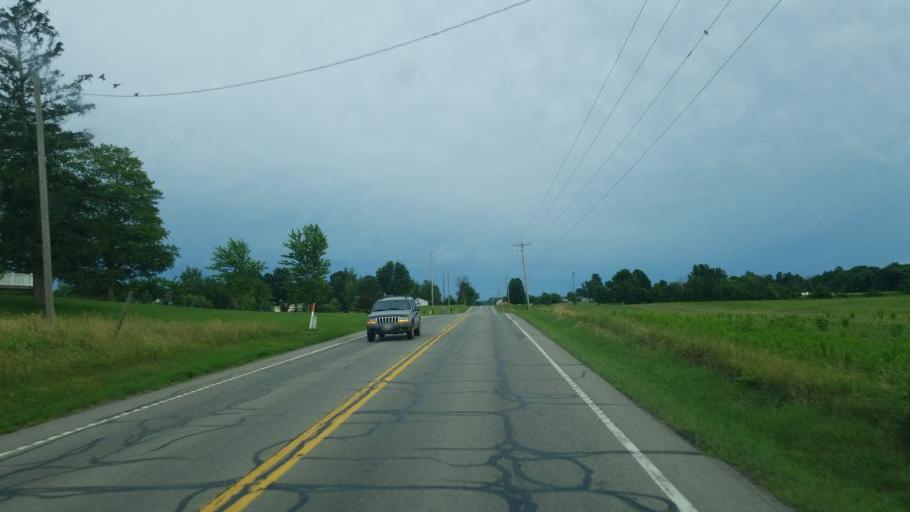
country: US
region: Ohio
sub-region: Huron County
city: Greenwich
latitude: 40.9305
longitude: -82.4964
